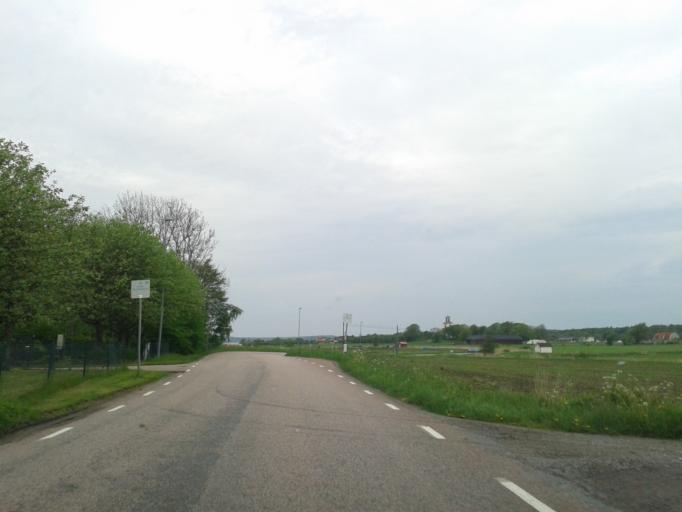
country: SE
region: Vaestra Goetaland
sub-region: Kungalvs Kommun
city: Kode
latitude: 57.8720
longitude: 11.7316
